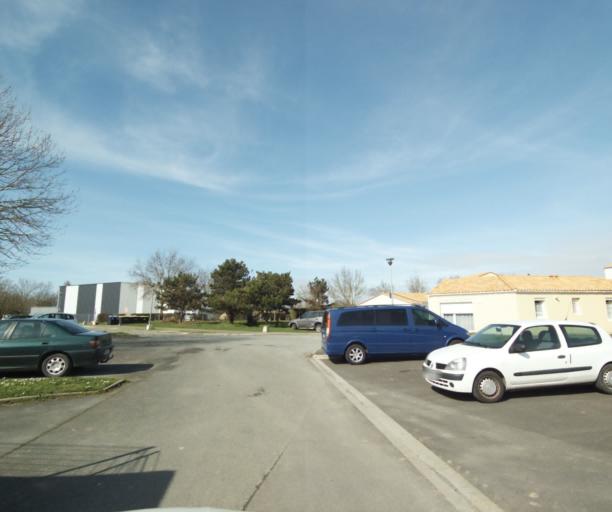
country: FR
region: Poitou-Charentes
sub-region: Departement de la Charente-Maritime
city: La Rochelle
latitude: 46.1726
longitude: -1.1728
